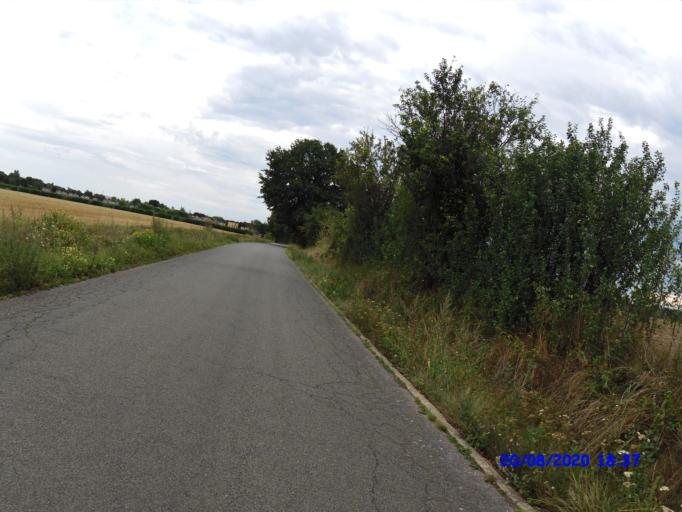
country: BE
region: Flanders
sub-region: Provincie Limburg
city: Sint-Truiden
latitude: 50.8353
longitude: 5.1760
